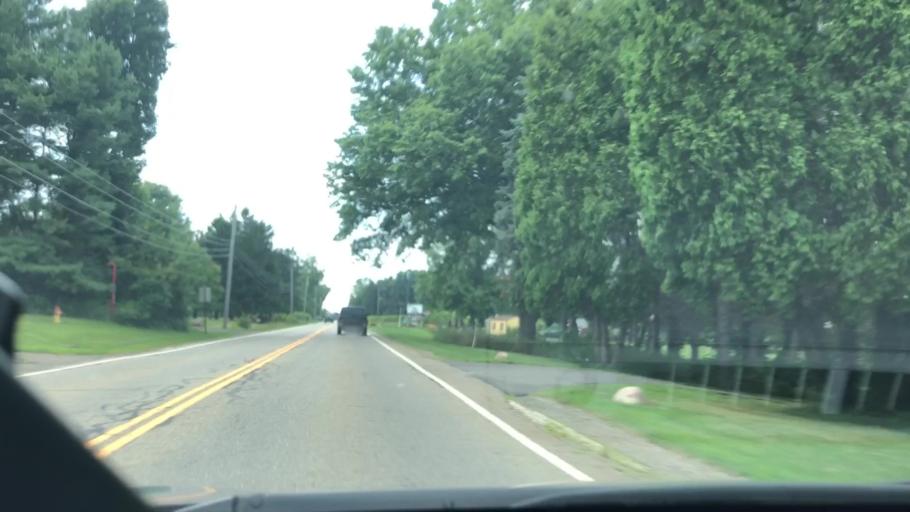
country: US
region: Ohio
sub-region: Summit County
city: Greensburg
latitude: 40.8798
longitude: -81.5038
